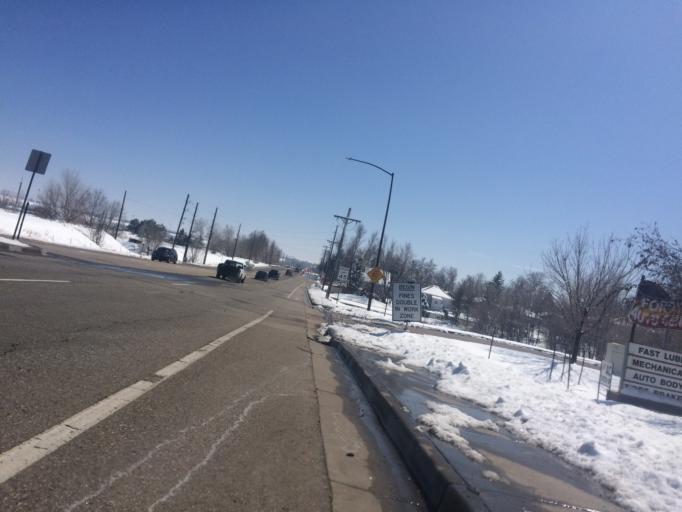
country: US
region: Colorado
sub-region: Boulder County
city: Louisville
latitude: 39.9861
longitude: -105.1282
